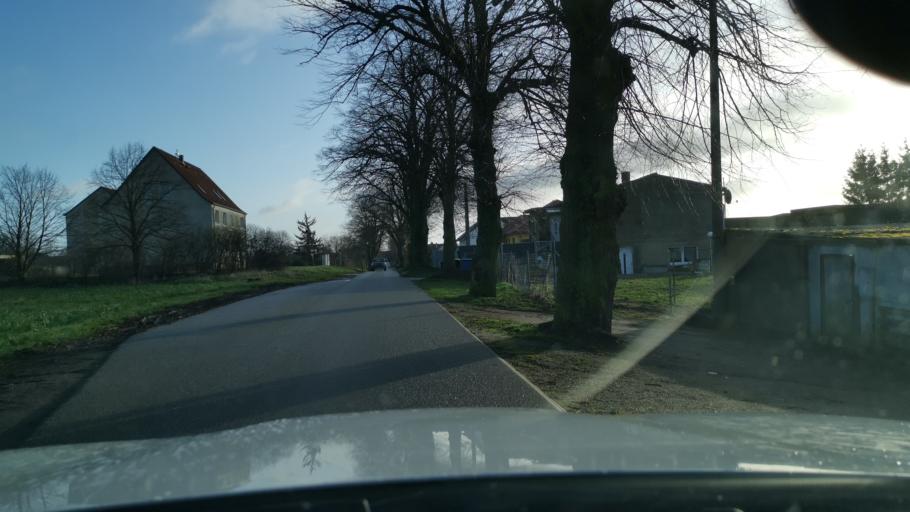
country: DE
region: Mecklenburg-Vorpommern
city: Laage
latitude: 53.9594
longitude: 12.3101
